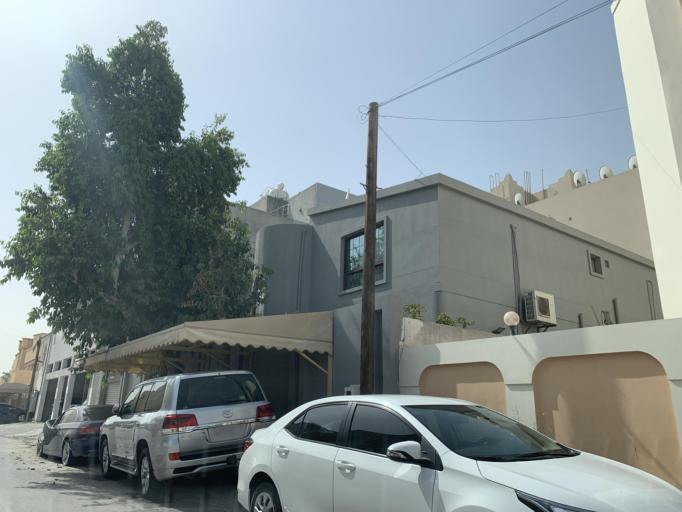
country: BH
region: Northern
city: Madinat `Isa
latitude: 26.1722
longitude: 50.5630
